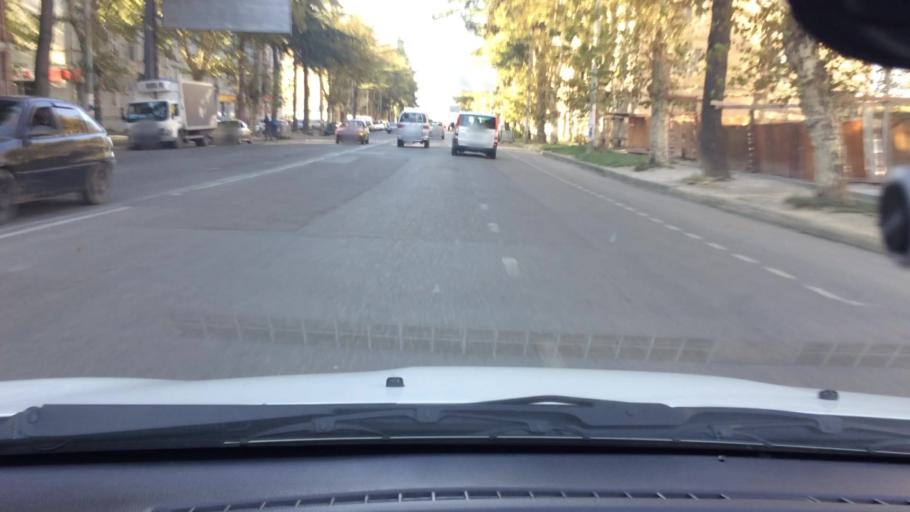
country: GE
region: Imereti
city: Kutaisi
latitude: 42.2604
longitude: 42.6714
